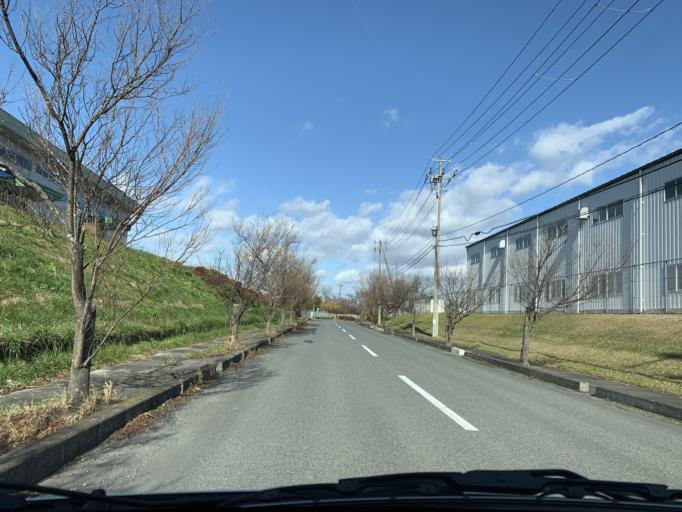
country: JP
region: Iwate
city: Mizusawa
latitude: 39.0304
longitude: 141.1133
